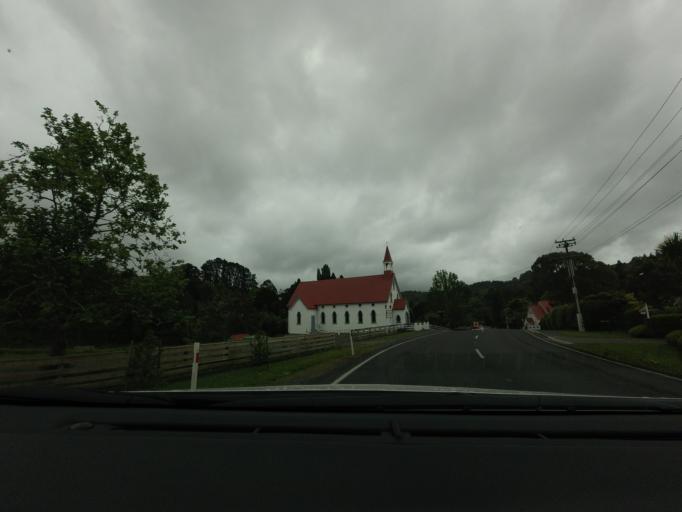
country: NZ
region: Auckland
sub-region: Auckland
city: Warkworth
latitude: -36.5149
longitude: 174.6622
